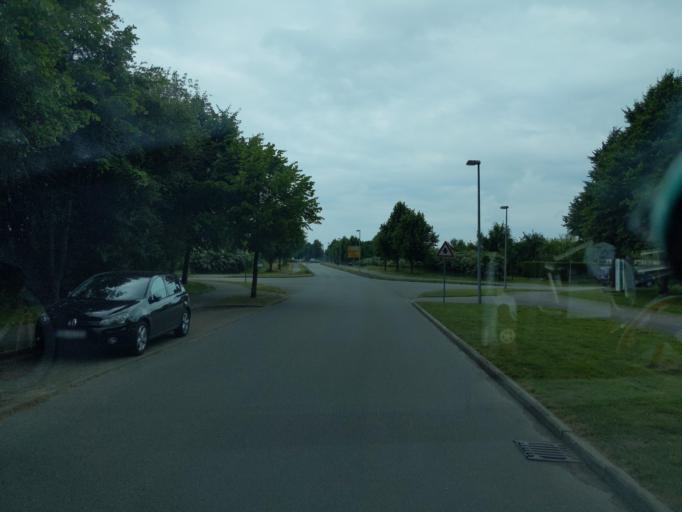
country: DE
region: Mecklenburg-Vorpommern
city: Ribnitz-Damgarten
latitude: 54.2369
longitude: 12.4421
